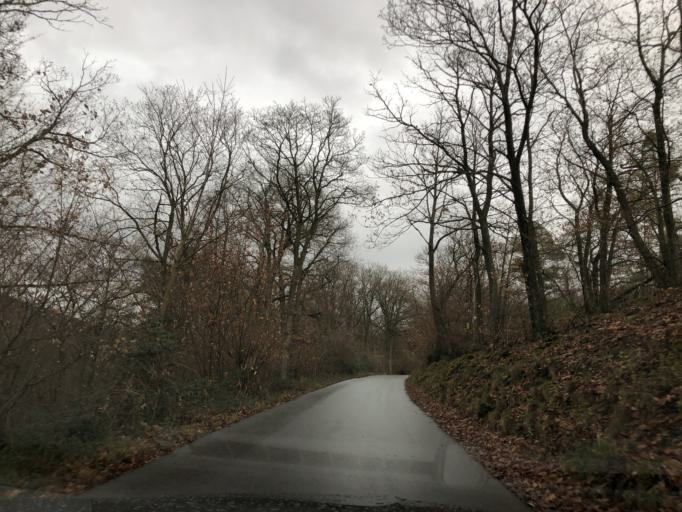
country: DE
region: Baden-Wuerttemberg
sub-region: Karlsruhe Region
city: Dossenheim
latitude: 49.4494
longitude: 8.6843
